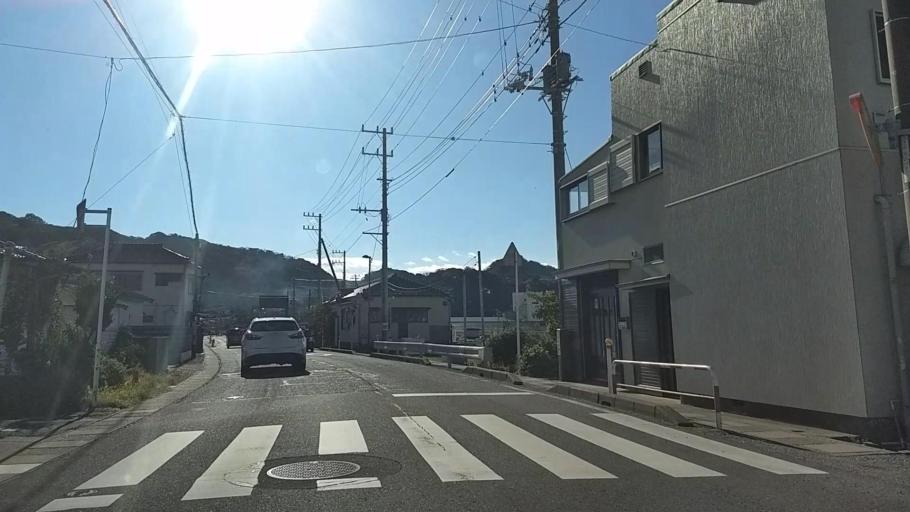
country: JP
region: Chiba
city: Tateyama
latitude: 35.1337
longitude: 139.8384
